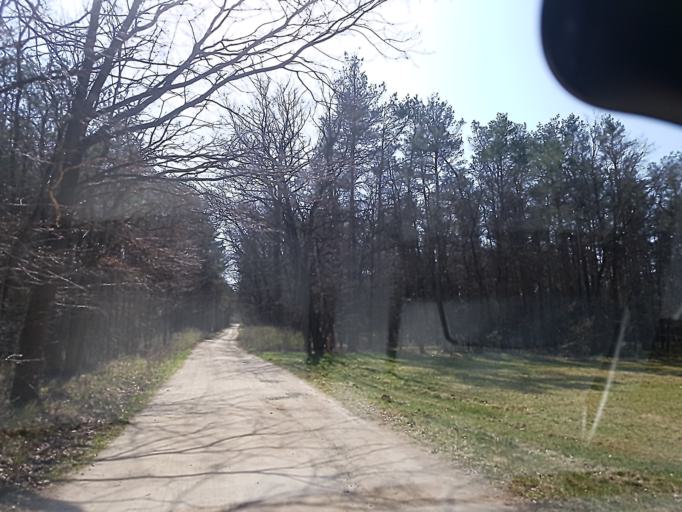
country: DE
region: Brandenburg
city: Doberlug-Kirchhain
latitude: 51.6317
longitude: 13.6073
